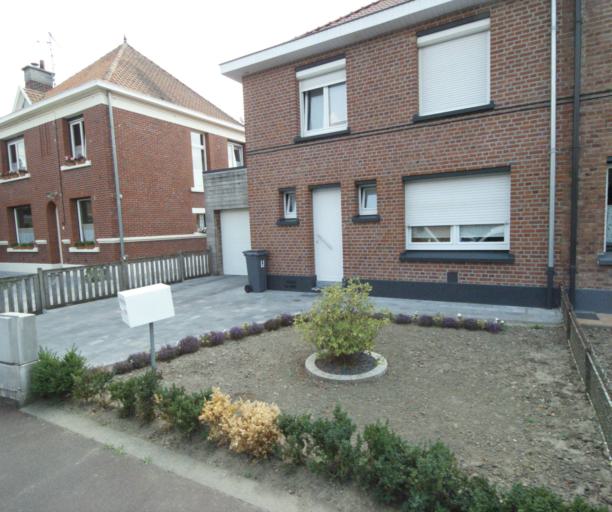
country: FR
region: Nord-Pas-de-Calais
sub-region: Departement du Nord
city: Comines
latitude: 50.7411
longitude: 3.0120
